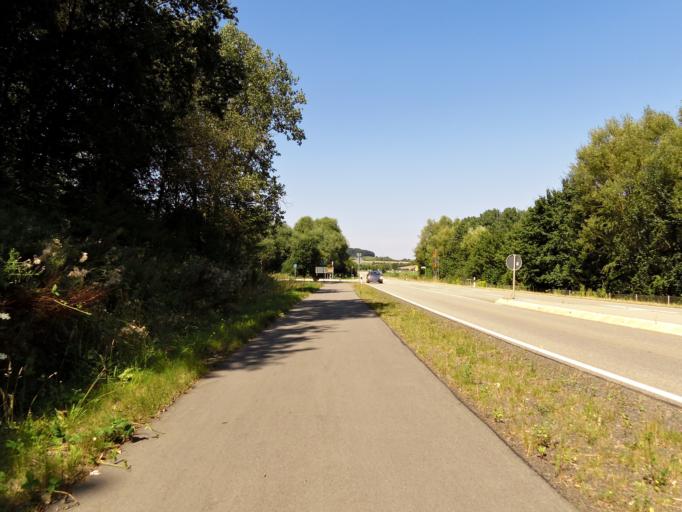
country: DE
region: Rheinland-Pfalz
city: Munchweiler an der Alsenz
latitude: 49.5278
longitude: 7.8878
